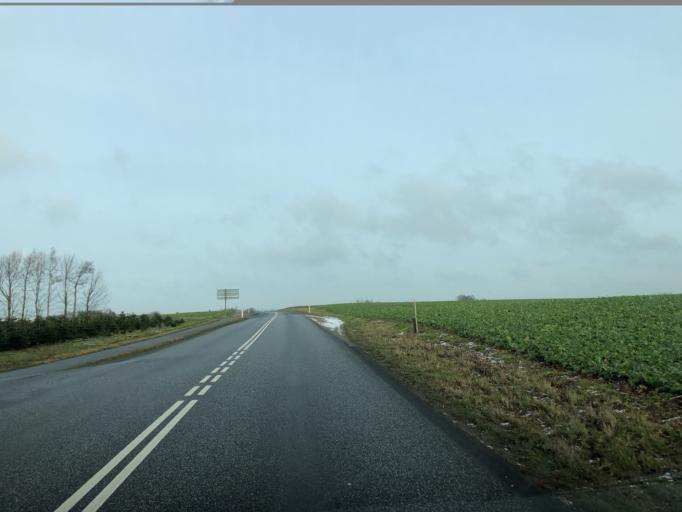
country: DK
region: South Denmark
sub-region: Vejle Kommune
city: Jelling
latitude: 55.7685
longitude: 9.4242
